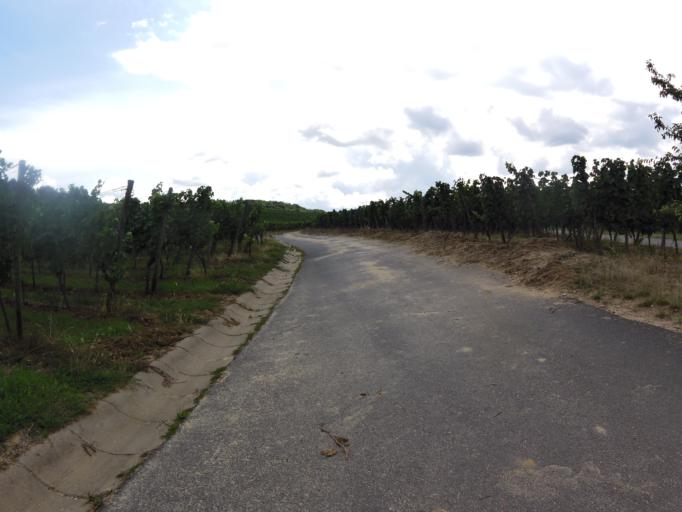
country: DE
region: Bavaria
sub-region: Regierungsbezirk Unterfranken
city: Sommerhausen
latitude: 49.6944
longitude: 10.0295
